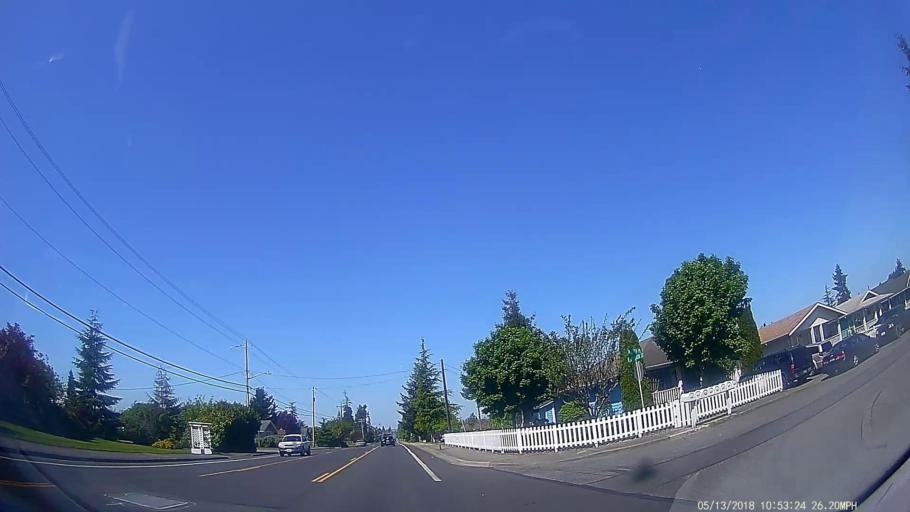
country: US
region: Washington
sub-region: Skagit County
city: Mount Vernon
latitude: 48.4210
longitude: -122.3026
